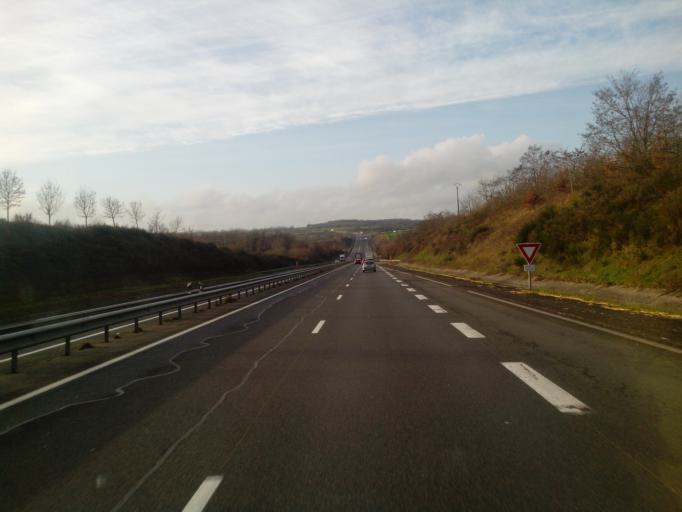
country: FR
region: Poitou-Charentes
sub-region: Departement des Deux-Sevres
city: Bressuire
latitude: 46.8554
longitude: -0.4842
